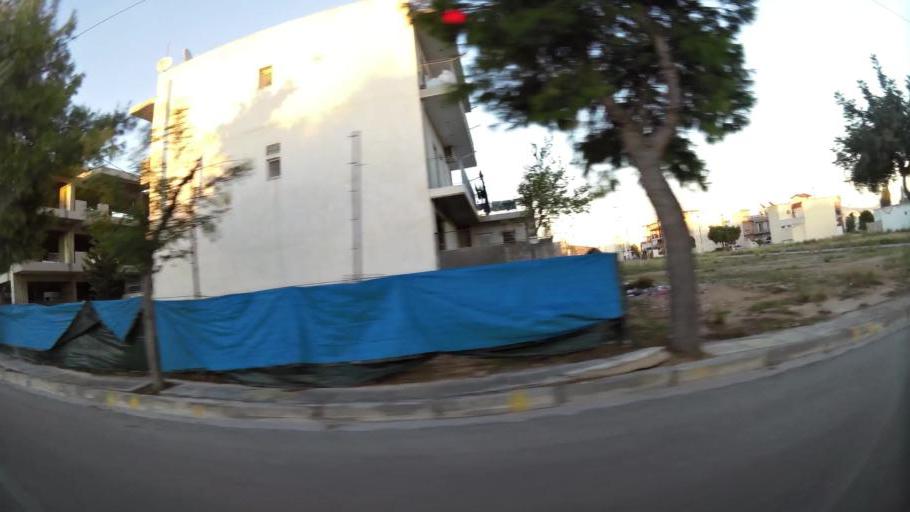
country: GR
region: Attica
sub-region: Nomarchia Dytikis Attikis
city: Ano Liosia
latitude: 38.0876
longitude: 23.6967
